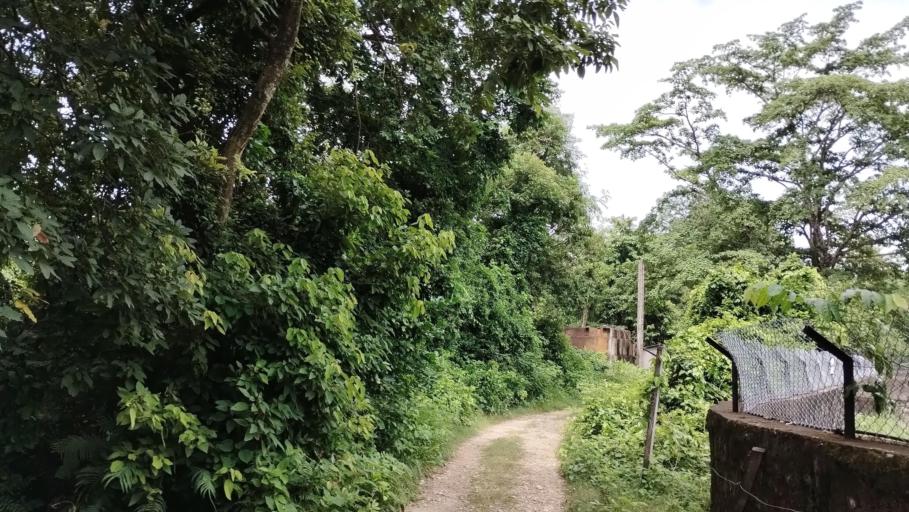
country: NP
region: Far Western
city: Tikapur
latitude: 28.4534
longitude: 81.2412
